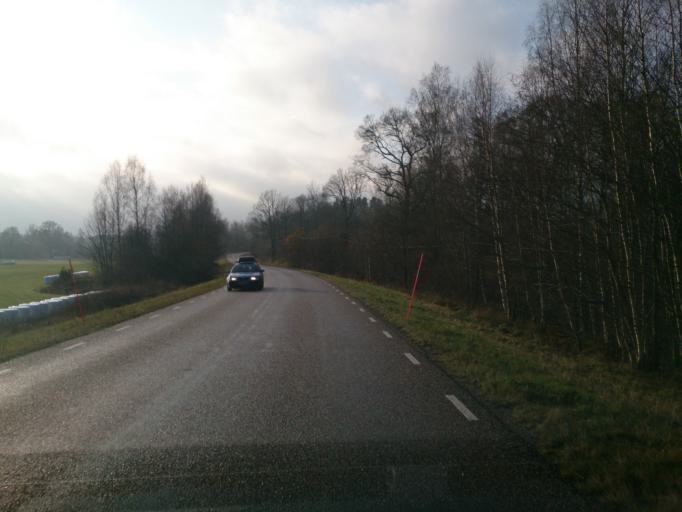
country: SE
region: OEstergoetland
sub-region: Atvidabergs Kommun
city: Atvidaberg
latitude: 58.2291
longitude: 15.9956
